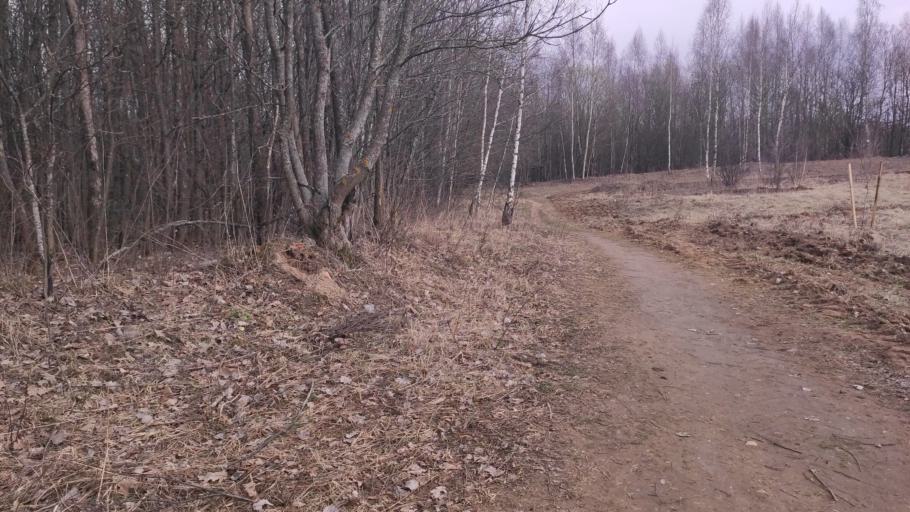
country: BY
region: Minsk
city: Novoye Medvezhino
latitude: 53.8899
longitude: 27.4697
